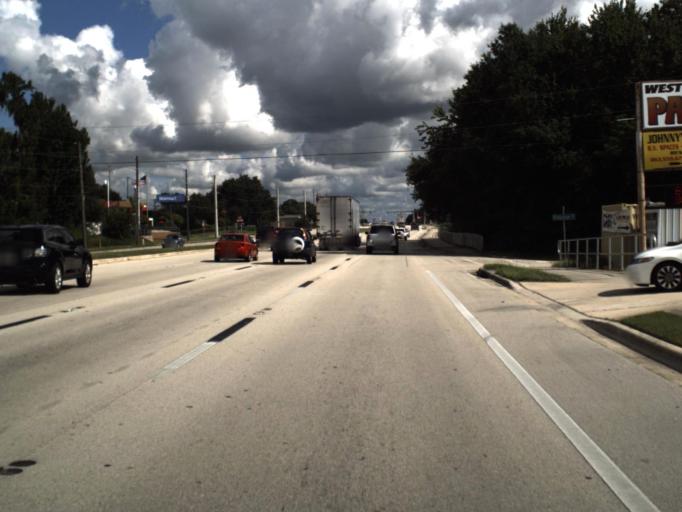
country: US
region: Florida
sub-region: Polk County
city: Gibsonia
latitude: 28.1160
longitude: -81.9736
